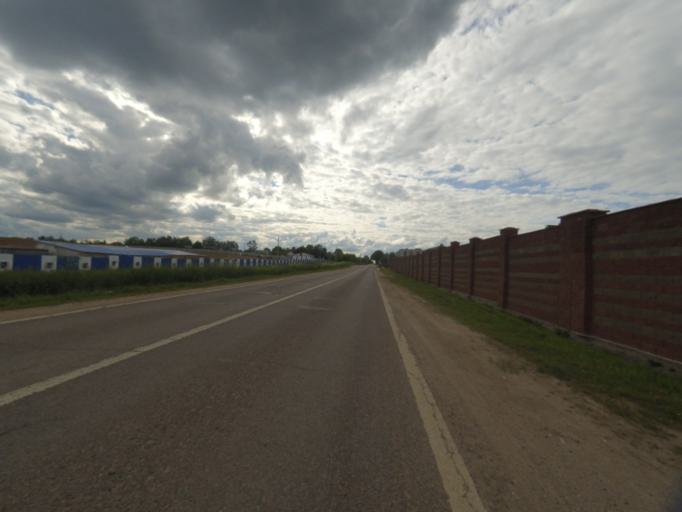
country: RU
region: Moskovskaya
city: Marfino
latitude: 56.1235
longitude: 37.5559
